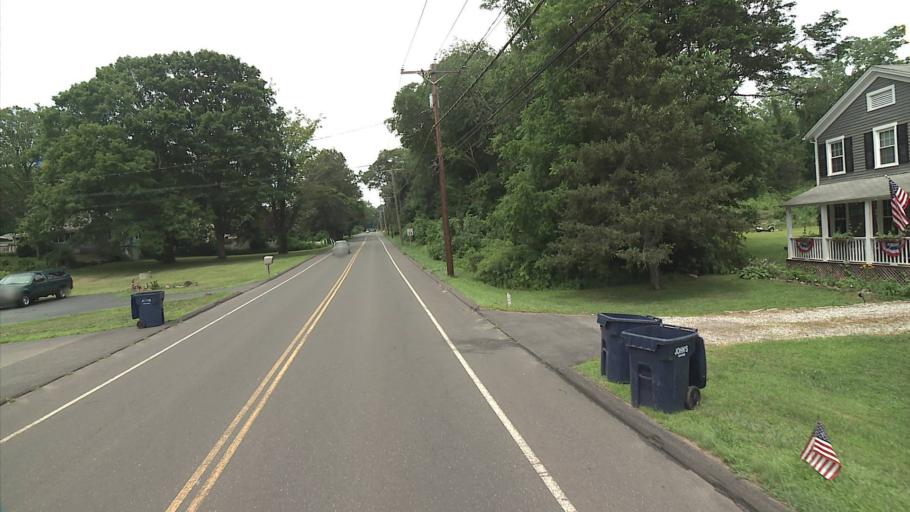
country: US
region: Connecticut
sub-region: New Haven County
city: Madison
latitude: 41.3055
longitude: -72.5909
